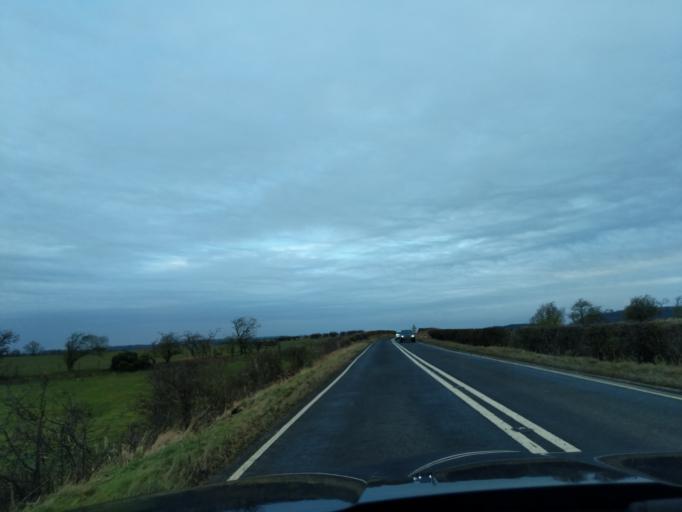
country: GB
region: England
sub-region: Northumberland
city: Rothley
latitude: 55.1161
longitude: -1.9011
